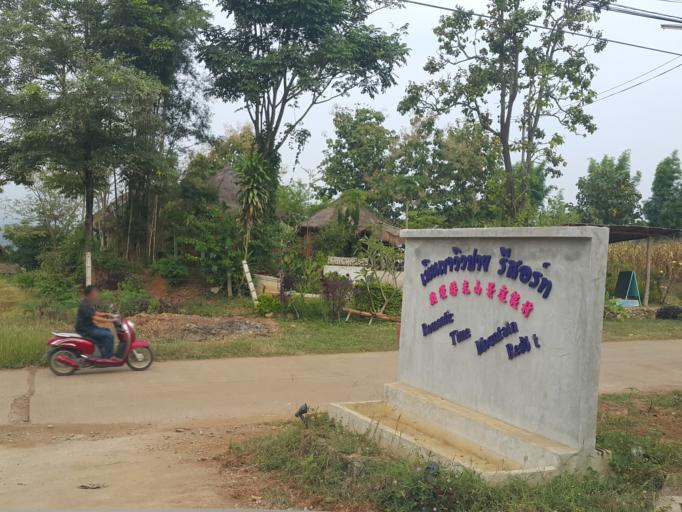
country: TH
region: Chiang Mai
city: Pai
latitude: 19.3643
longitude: 98.4498
